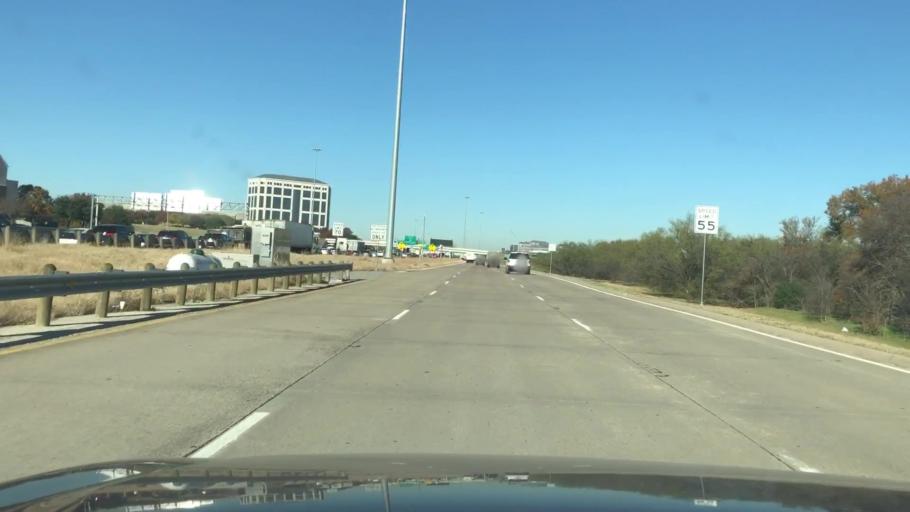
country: US
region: Texas
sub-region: Dallas County
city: Farmers Branch
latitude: 32.8843
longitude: -96.9508
